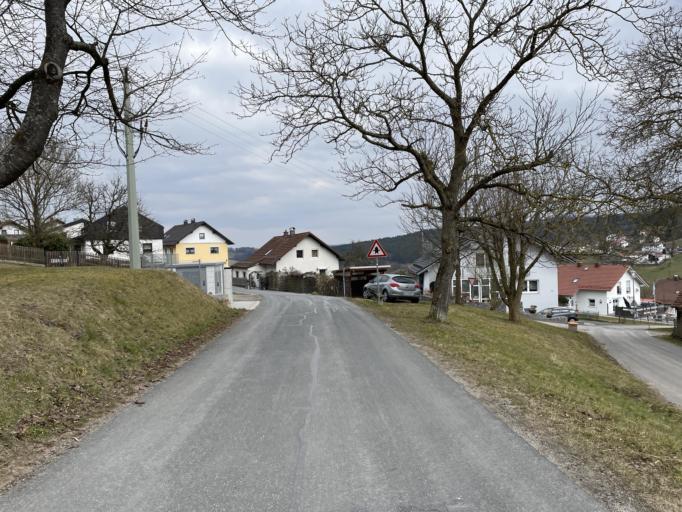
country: DE
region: Bavaria
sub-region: Upper Palatinate
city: Runding
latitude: 49.2172
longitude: 12.7653
